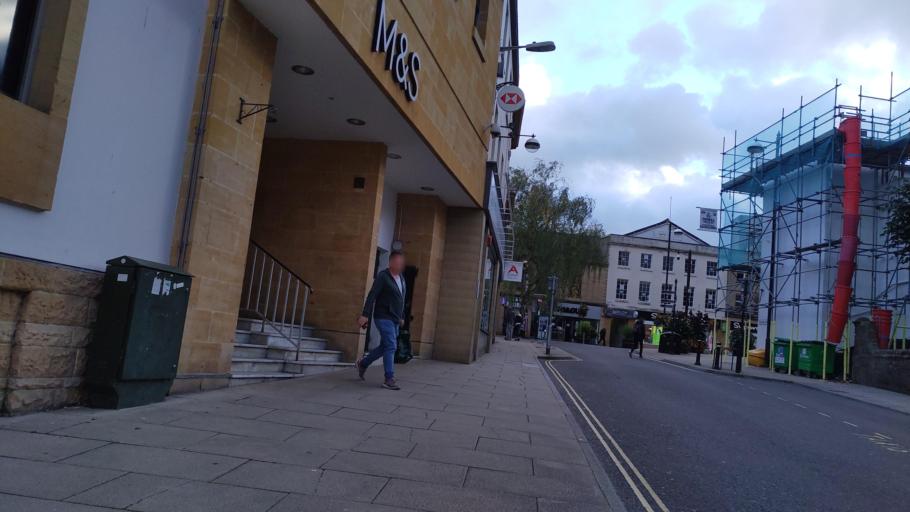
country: GB
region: England
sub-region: Somerset
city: Yeovil
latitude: 50.9419
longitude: -2.6319
